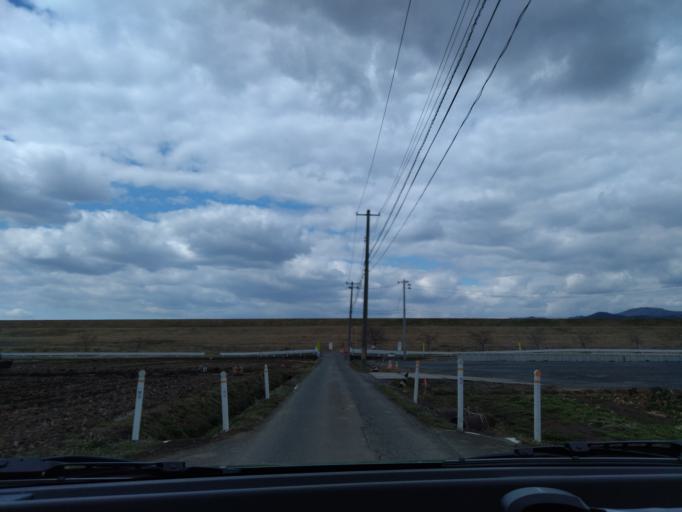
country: JP
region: Iwate
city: Ichinoseki
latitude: 38.9415
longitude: 141.1417
